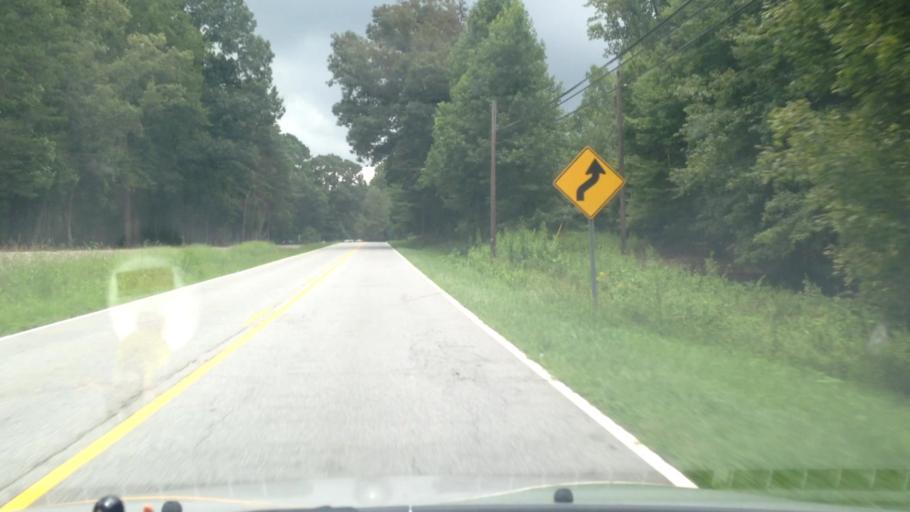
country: US
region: North Carolina
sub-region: Forsyth County
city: Walkertown
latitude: 36.2190
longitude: -80.1673
